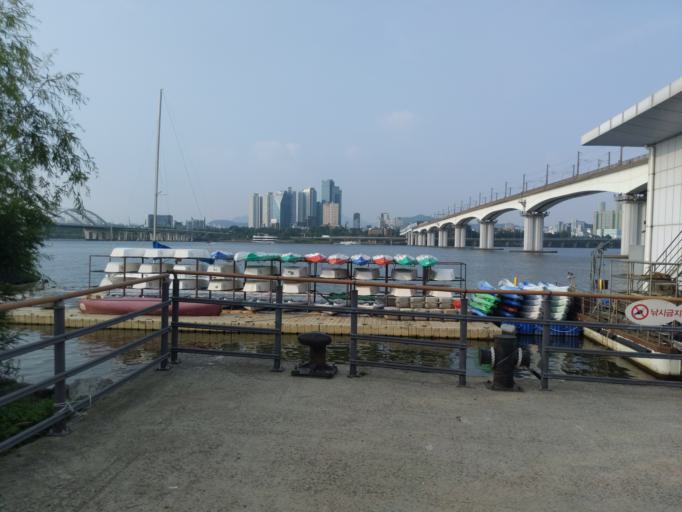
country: KR
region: Gyeonggi-do
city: Kwangmyong
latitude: 37.5381
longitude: 126.9044
